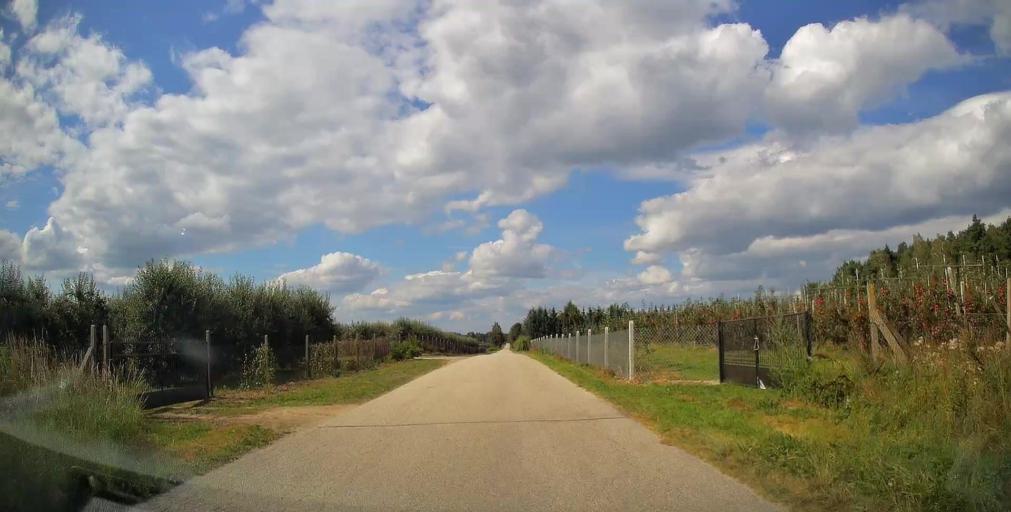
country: PL
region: Masovian Voivodeship
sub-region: Powiat grojecki
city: Goszczyn
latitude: 51.7041
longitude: 20.8965
